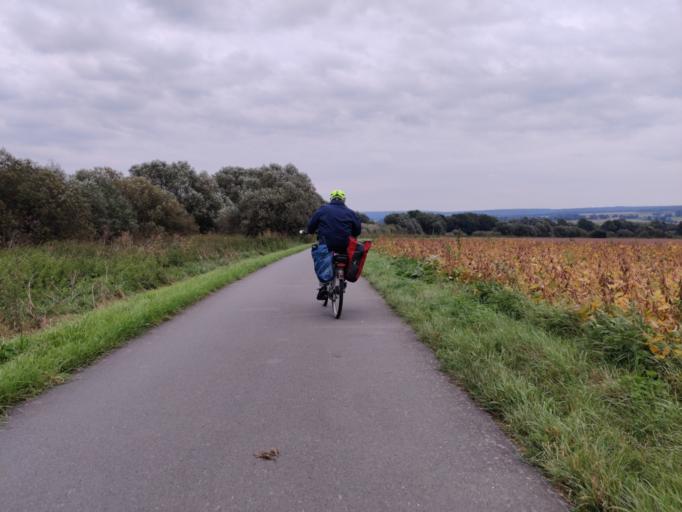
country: DE
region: Lower Saxony
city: Holzminden
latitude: 51.8069
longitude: 9.4178
